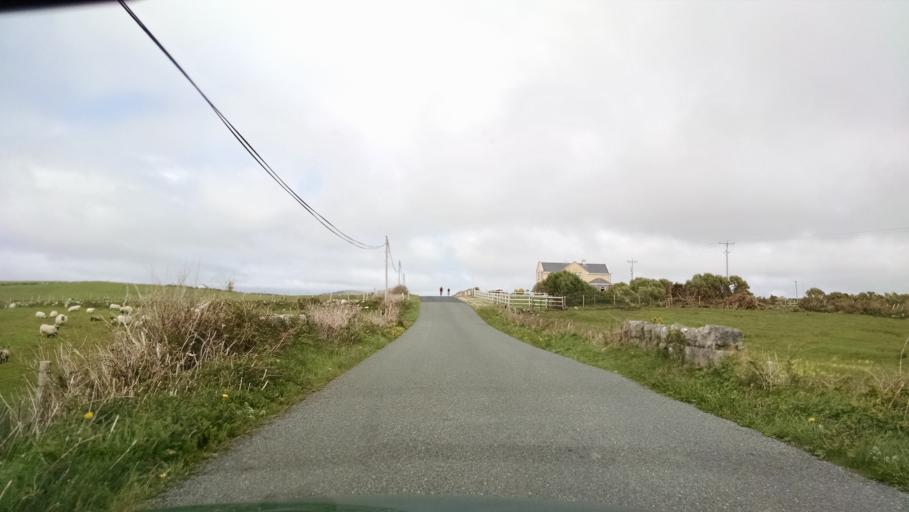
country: IE
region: Connaught
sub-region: County Galway
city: Clifden
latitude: 53.7157
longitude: -9.8790
